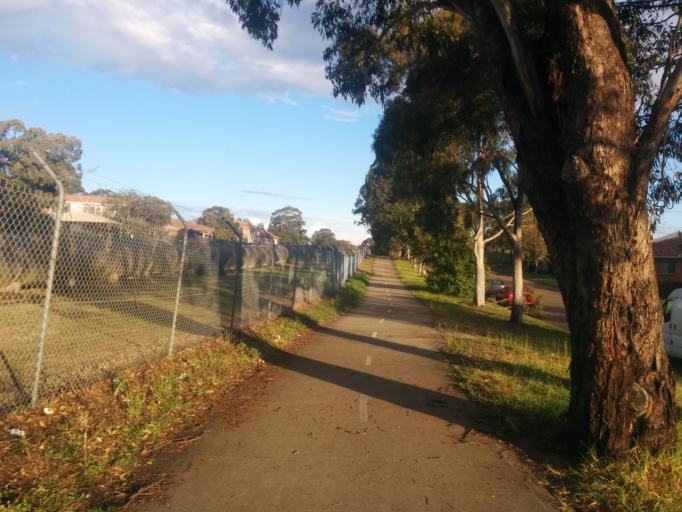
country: AU
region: New South Wales
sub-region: Holroyd
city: Guildford West
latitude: -33.8540
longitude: 150.9784
